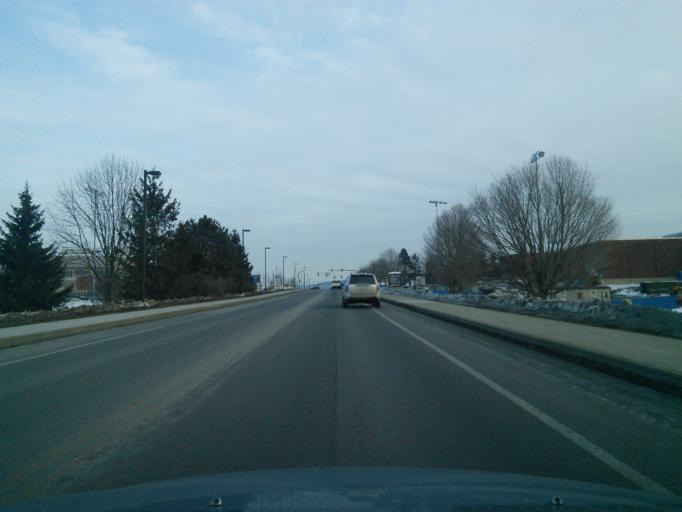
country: US
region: Pennsylvania
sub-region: Centre County
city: State College
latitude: 40.8093
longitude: -77.8601
